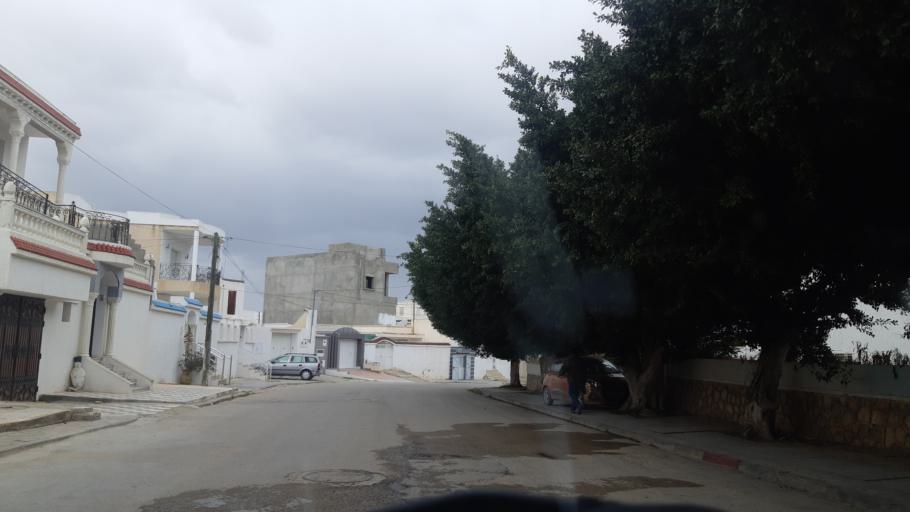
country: TN
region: Susah
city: Akouda
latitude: 35.8672
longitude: 10.5486
